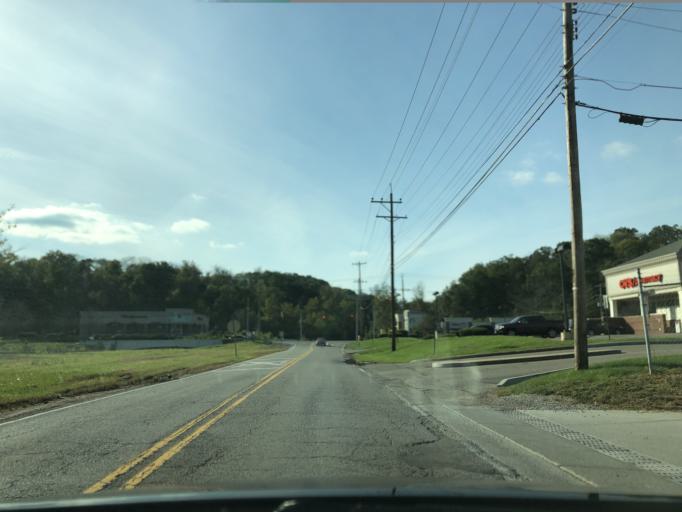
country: US
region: Ohio
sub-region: Hamilton County
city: The Village of Indian Hill
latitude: 39.2505
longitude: -84.2949
